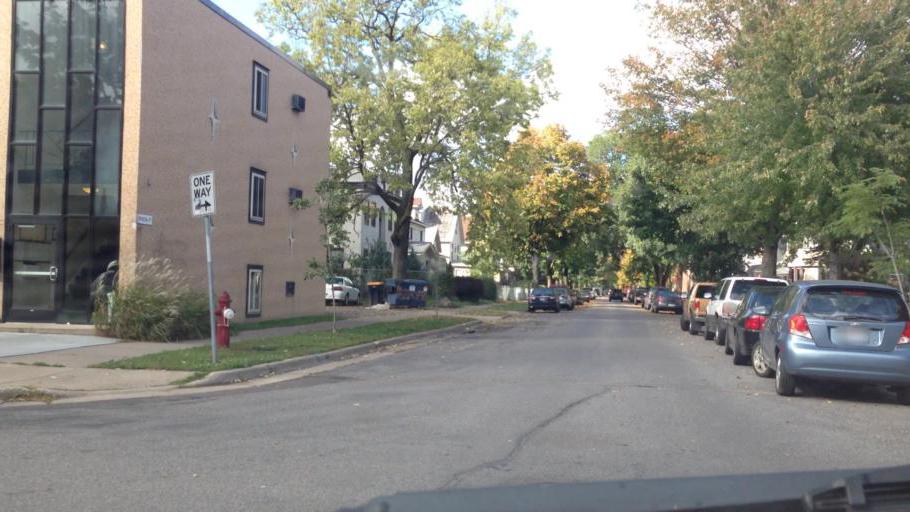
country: US
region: Minnesota
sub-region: Hennepin County
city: Minneapolis
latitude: 44.9519
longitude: -93.2855
